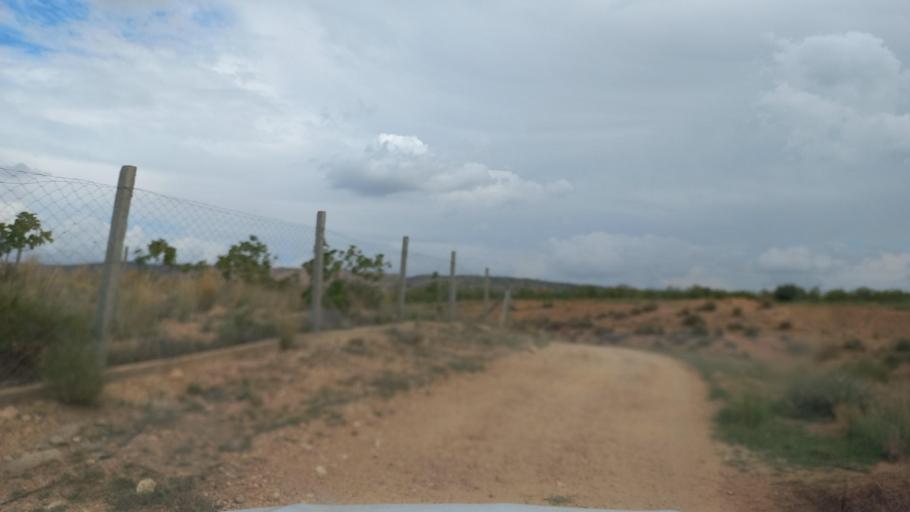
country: TN
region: Al Qasrayn
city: Sbiba
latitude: 35.3110
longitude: 9.1068
